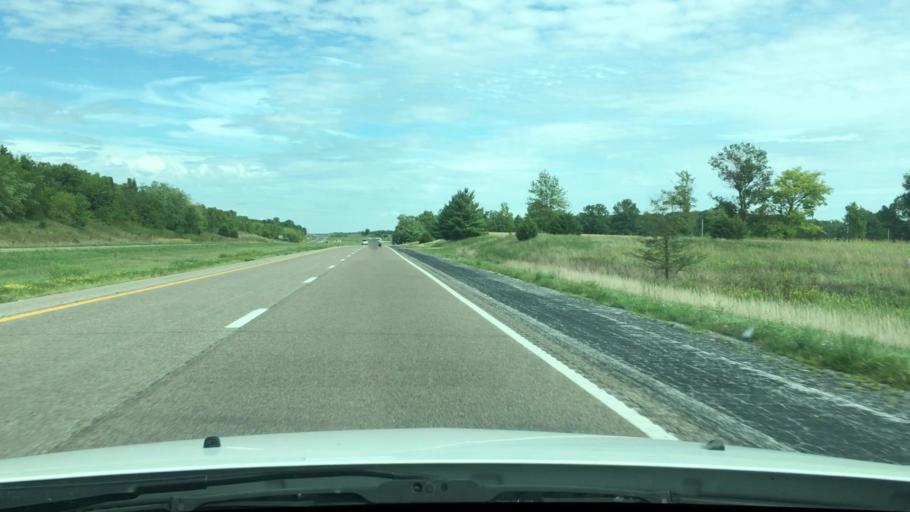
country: US
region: Missouri
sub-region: Audrain County
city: Mexico
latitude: 39.0533
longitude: -91.8941
